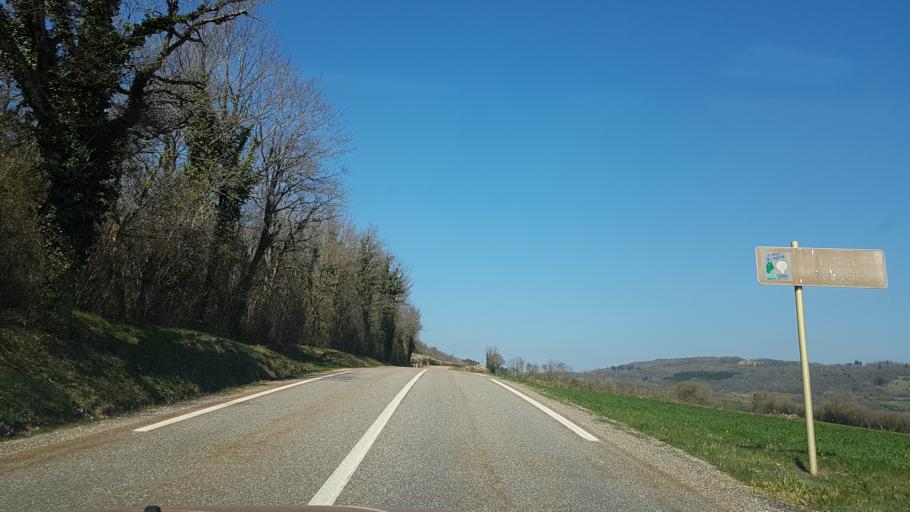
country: FR
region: Franche-Comte
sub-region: Departement du Jura
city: Orgelet
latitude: 46.5291
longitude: 5.6411
